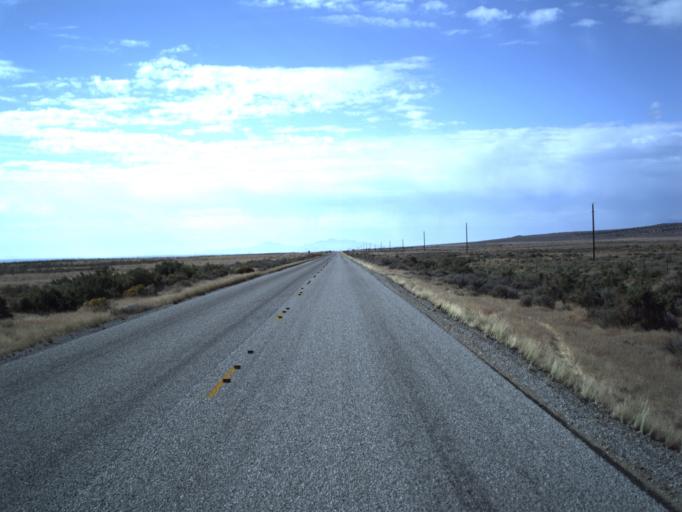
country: US
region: Utah
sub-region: Tooele County
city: Wendover
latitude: 41.5531
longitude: -113.5859
